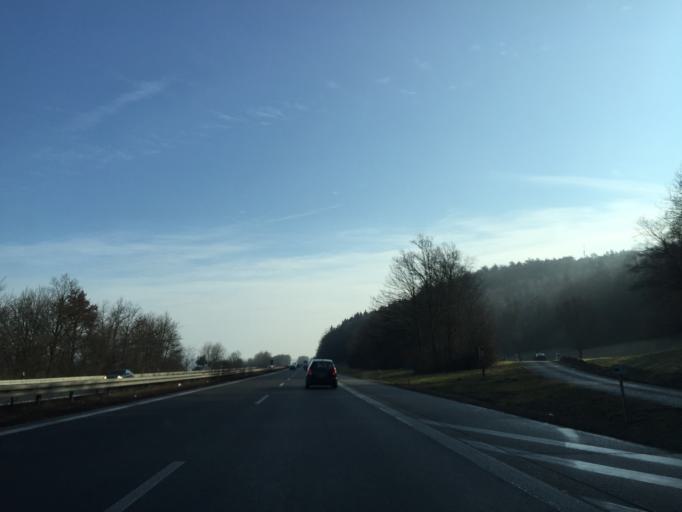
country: DE
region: Bavaria
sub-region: Regierungsbezirk Mittelfranken
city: Burghaslach
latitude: 49.7591
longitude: 10.5779
